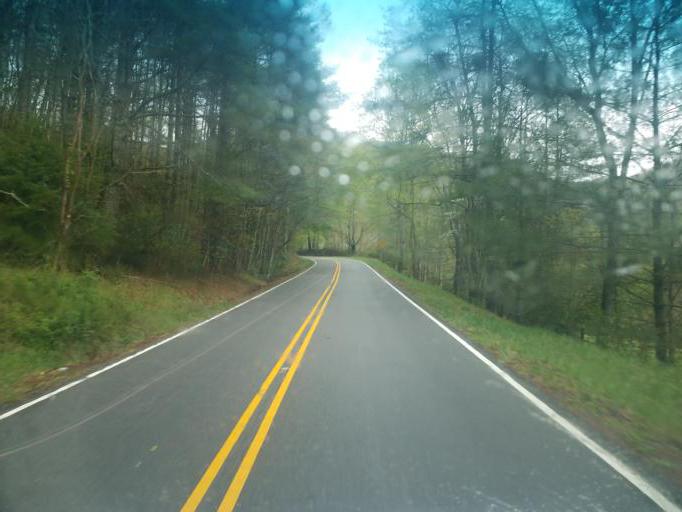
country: US
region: Virginia
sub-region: Washington County
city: Glade Spring
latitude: 36.6369
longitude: -81.7492
